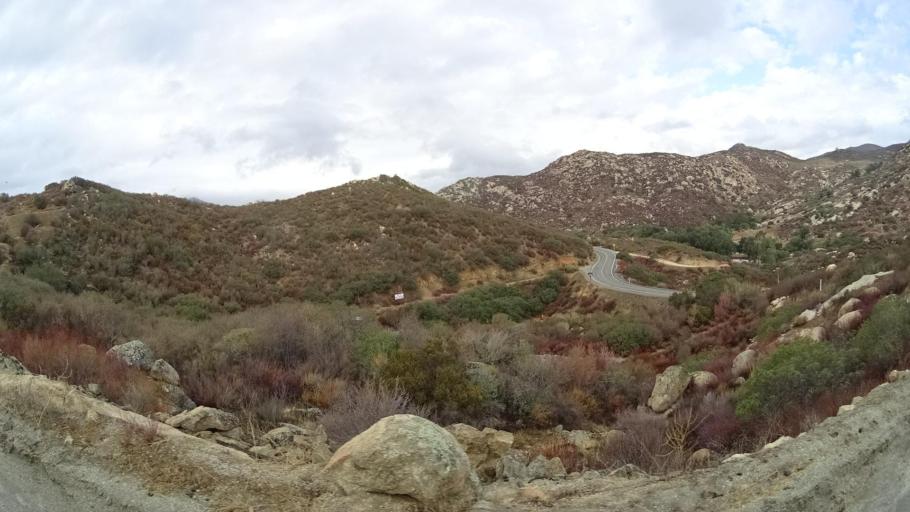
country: MX
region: Baja California
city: Tecate
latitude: 32.6001
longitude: -116.6393
